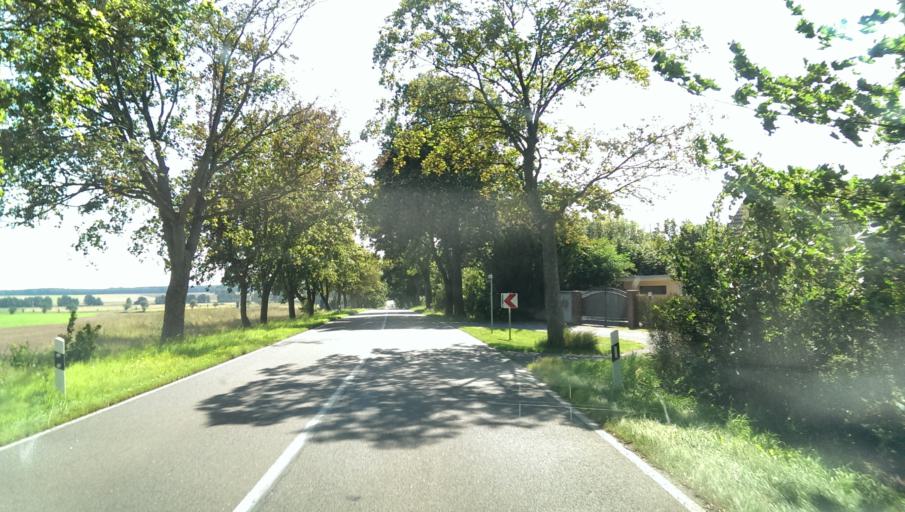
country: DE
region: Saxony-Anhalt
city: Kropstadt
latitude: 51.9741
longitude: 12.7580
